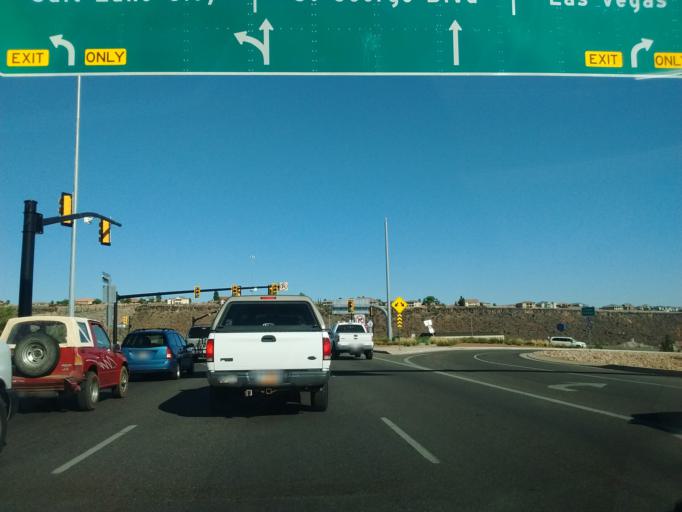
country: US
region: Utah
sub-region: Washington County
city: Saint George
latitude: 37.1097
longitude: -113.5600
